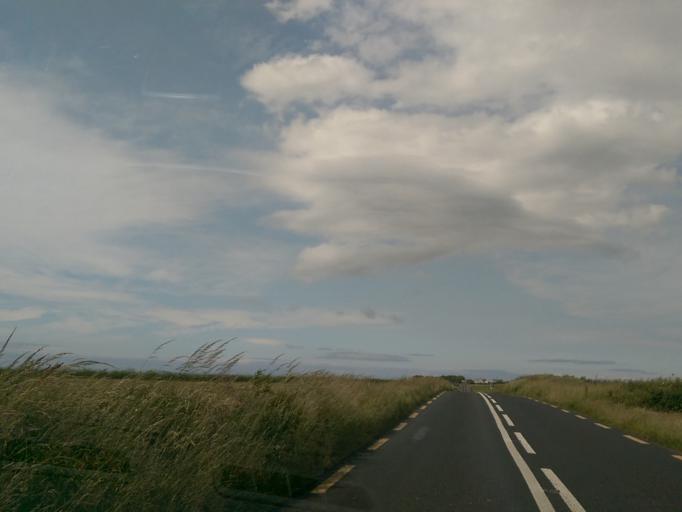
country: IE
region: Munster
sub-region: An Clar
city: Kilrush
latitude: 52.8016
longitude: -9.4490
